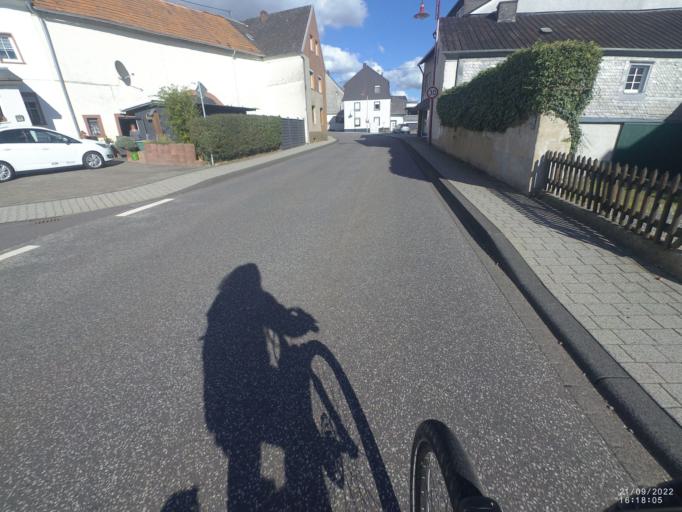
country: DE
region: Rheinland-Pfalz
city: Mehren
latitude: 50.1760
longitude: 6.8794
